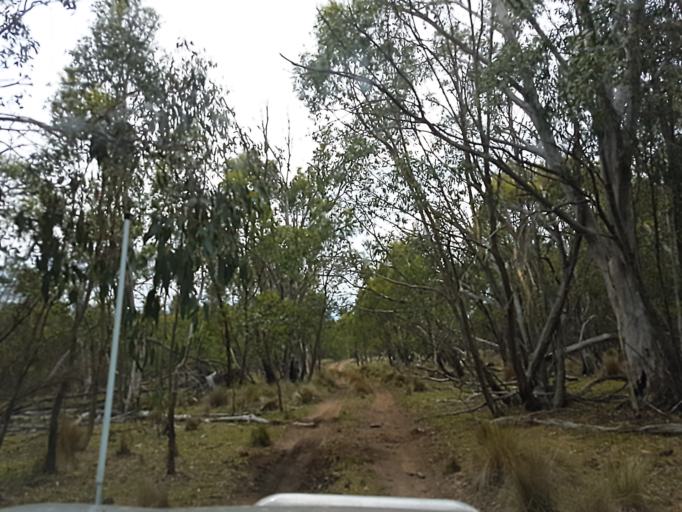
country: AU
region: New South Wales
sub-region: Snowy River
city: Jindabyne
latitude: -36.8542
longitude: 148.2608
